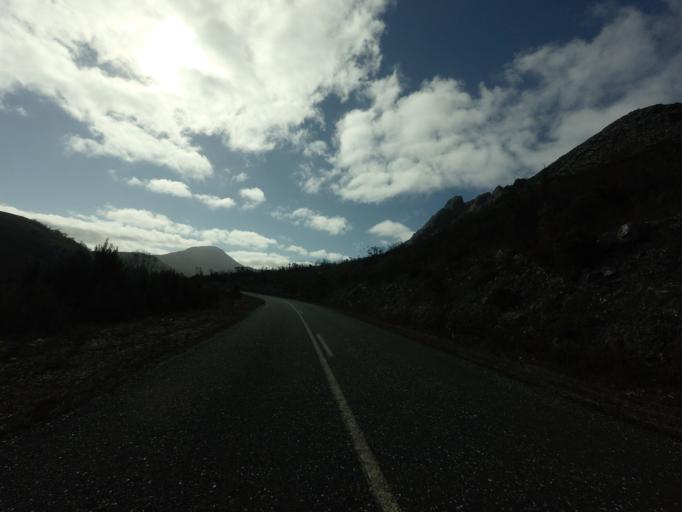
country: AU
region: Tasmania
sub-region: Huon Valley
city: Geeveston
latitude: -42.8616
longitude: 146.2225
